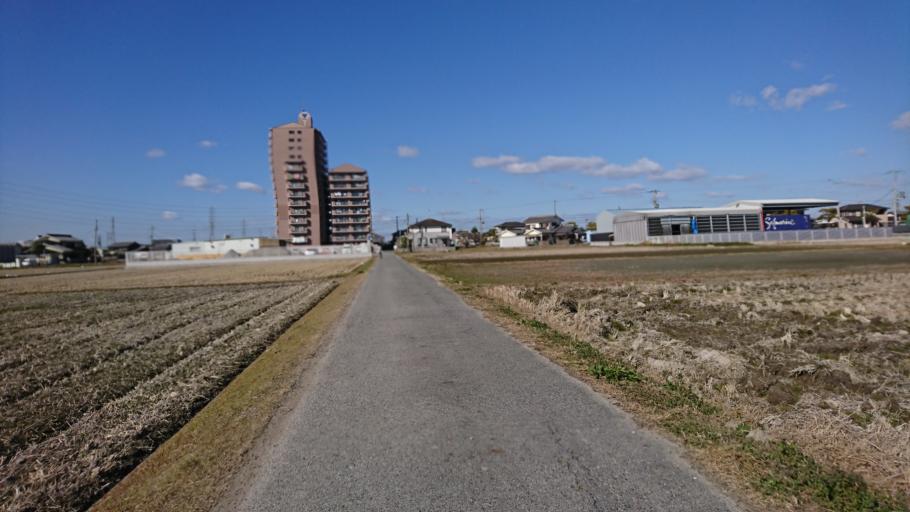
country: JP
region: Hyogo
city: Kakogawacho-honmachi
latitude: 34.7277
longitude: 134.8591
